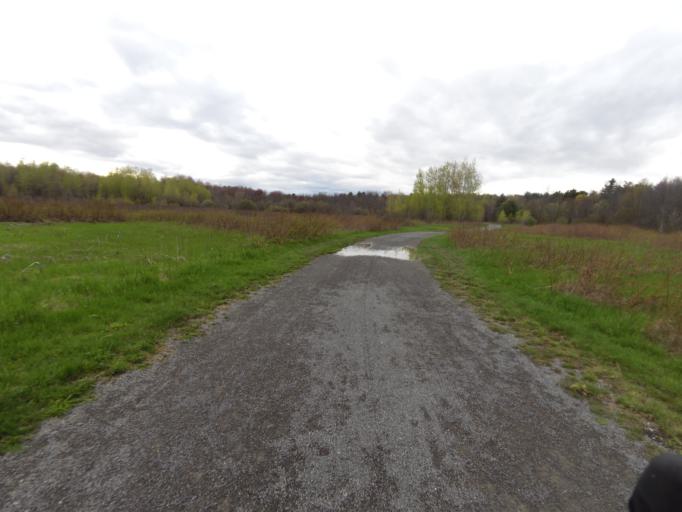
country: CA
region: Ontario
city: Bells Corners
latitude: 45.3170
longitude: -75.7930
